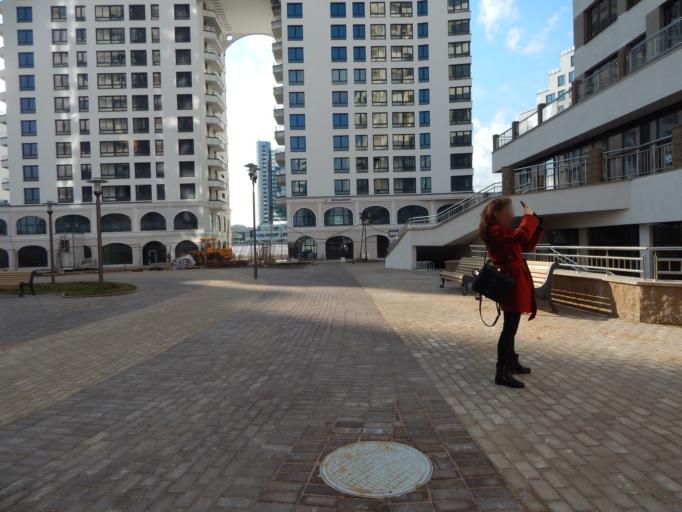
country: BY
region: Minsk
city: Borovlyany
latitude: 53.9315
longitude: 27.6514
